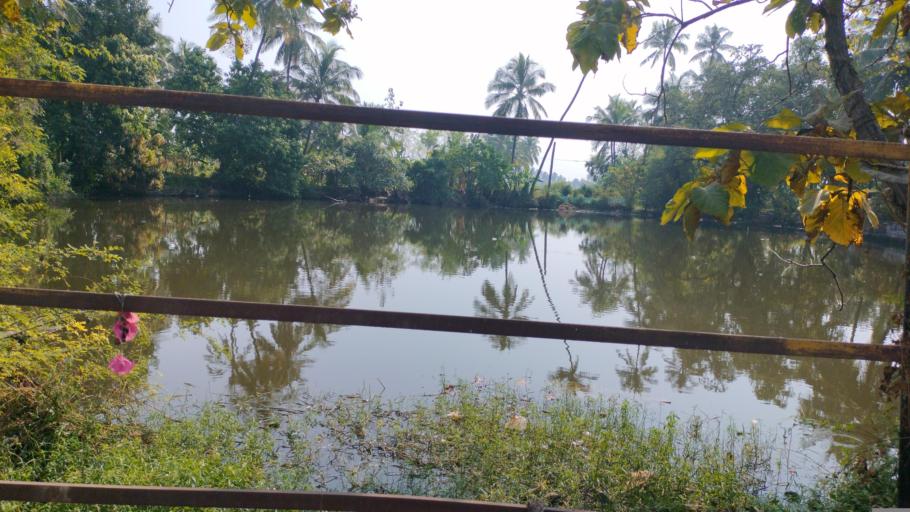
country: IN
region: Maharashtra
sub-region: Thane
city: Virar
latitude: 19.4085
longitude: 72.7865
